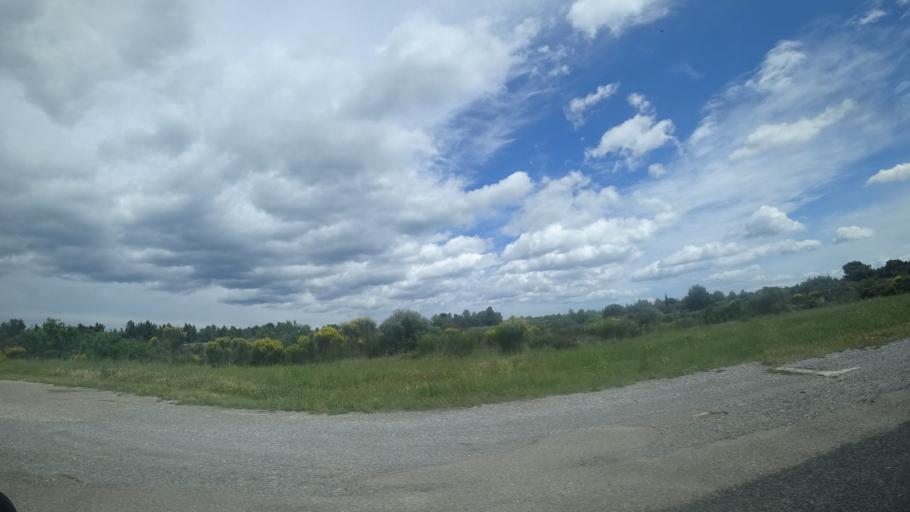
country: FR
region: Languedoc-Roussillon
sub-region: Departement de l'Aude
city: Leucate
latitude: 42.9236
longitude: 3.0181
